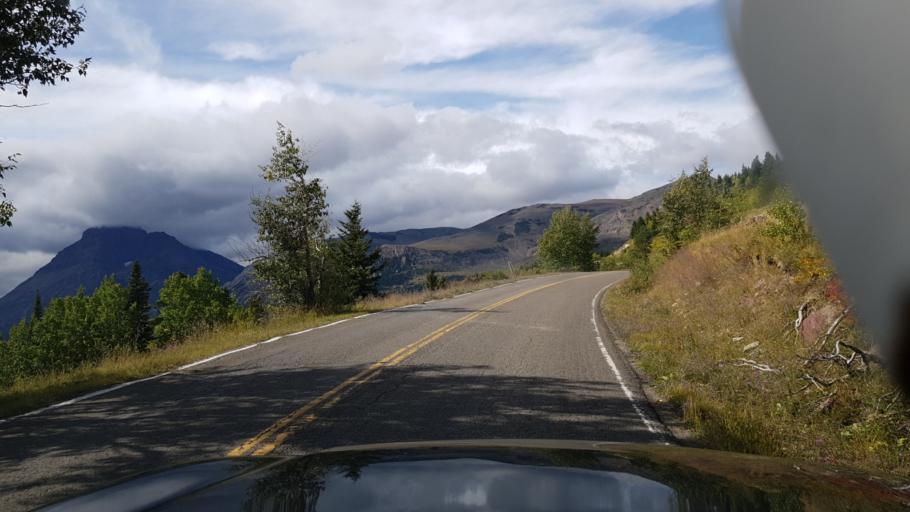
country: US
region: Montana
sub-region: Glacier County
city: South Browning
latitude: 48.5212
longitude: -113.2939
